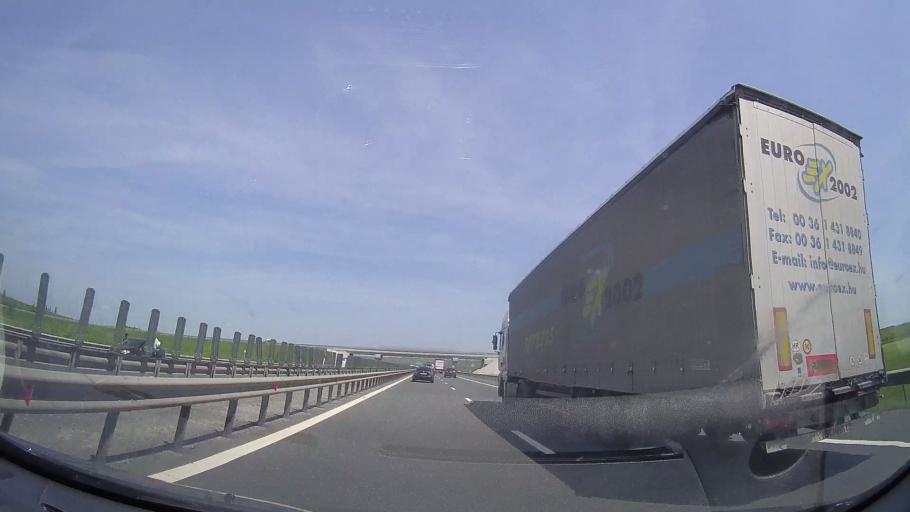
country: RO
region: Sibiu
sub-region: Comuna Sura Mica
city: Sura Mica
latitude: 45.8102
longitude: 24.0649
